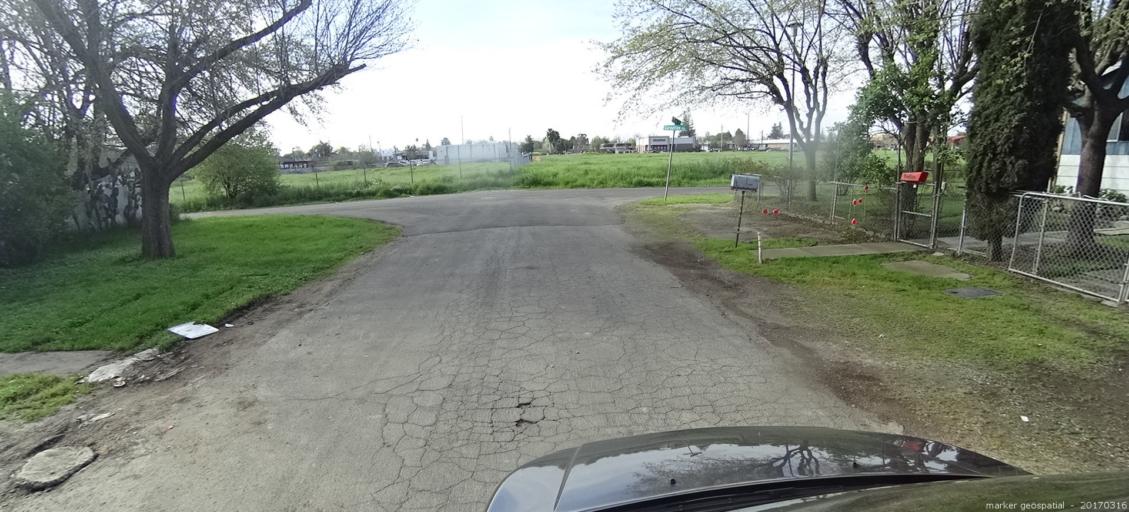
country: US
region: California
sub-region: Sacramento County
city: Parkway
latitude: 38.4980
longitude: -121.4756
